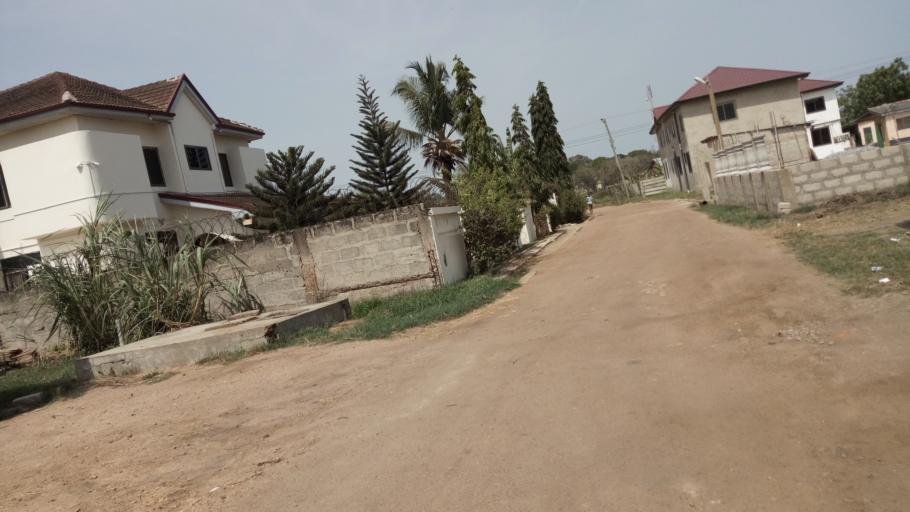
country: GH
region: Central
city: Winneba
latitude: 5.3594
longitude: -0.6361
